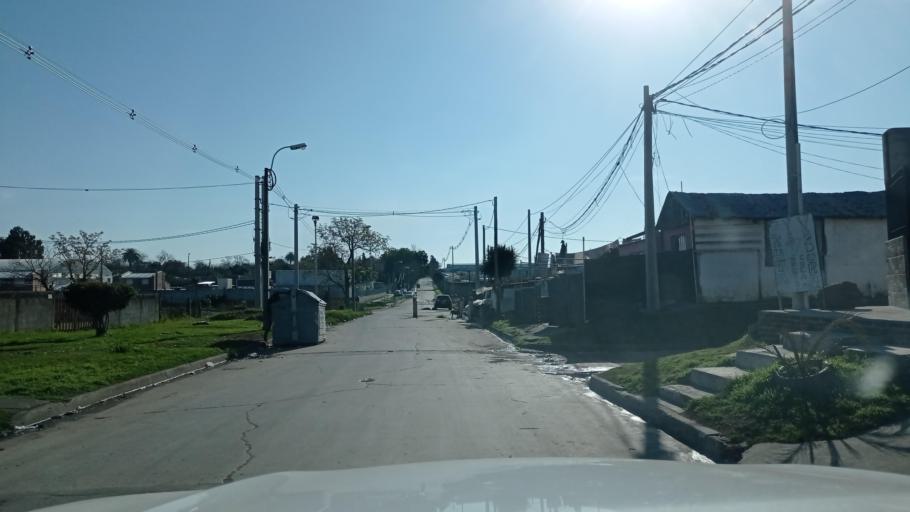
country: UY
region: Canelones
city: La Paz
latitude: -34.8381
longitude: -56.2425
